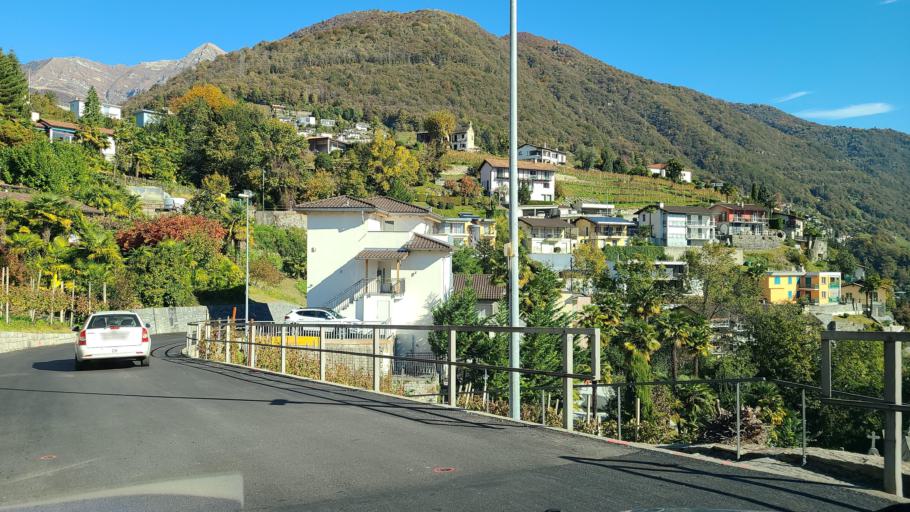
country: CH
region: Ticino
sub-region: Locarno District
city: Gordola
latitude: 46.1821
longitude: 8.8439
